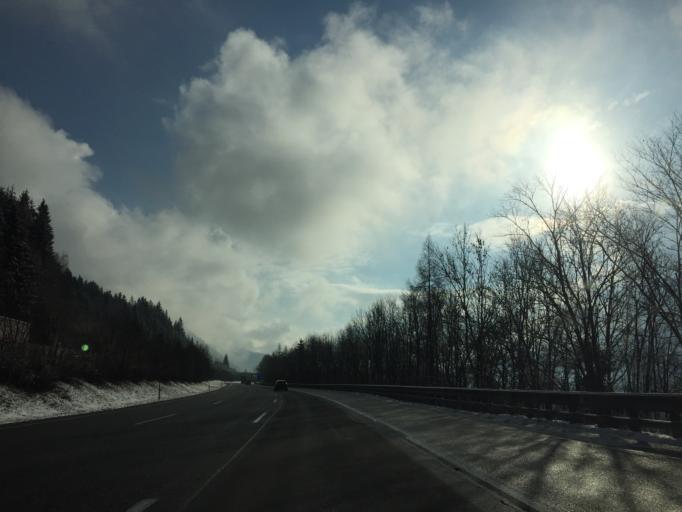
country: AT
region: Salzburg
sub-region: Politischer Bezirk Sankt Johann im Pongau
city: Werfenweng
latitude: 47.4357
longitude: 13.2451
